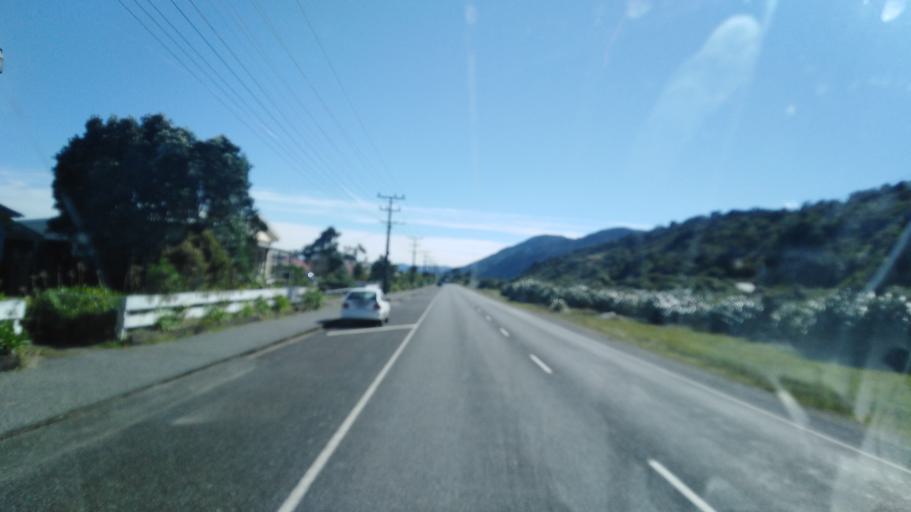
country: NZ
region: West Coast
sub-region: Buller District
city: Westport
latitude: -41.6220
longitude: 171.8610
